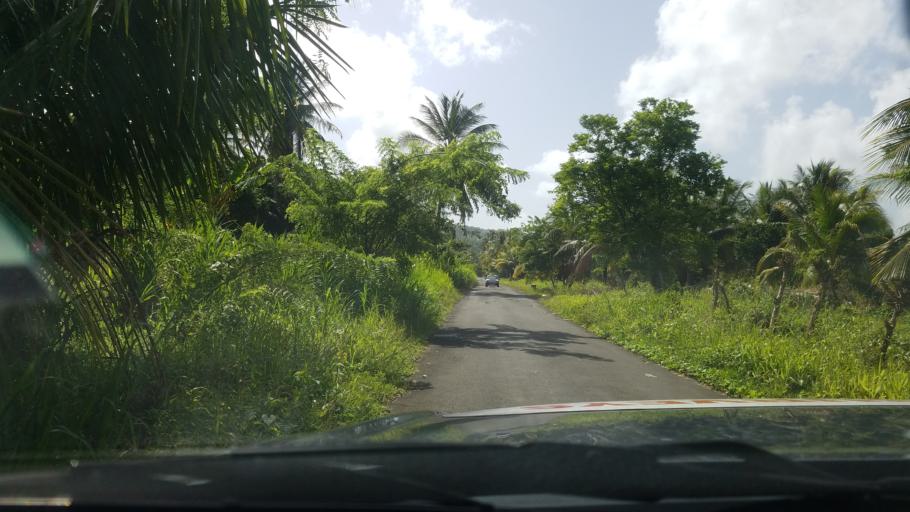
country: LC
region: Anse-la-Raye
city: Anse La Raye
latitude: 13.9558
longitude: -61.0101
